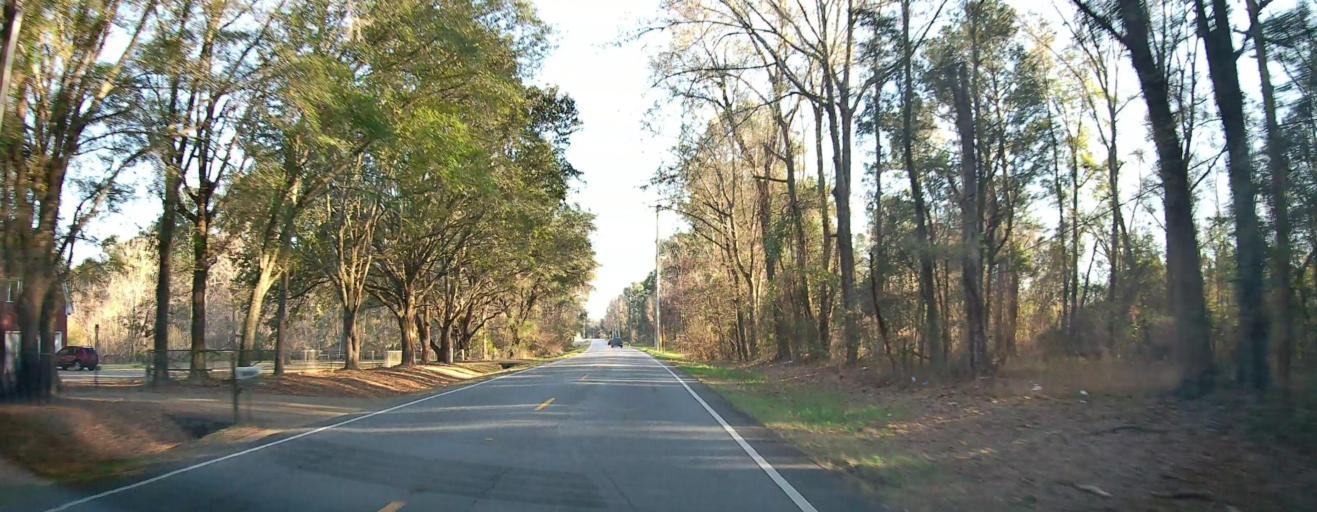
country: US
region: Georgia
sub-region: Dougherty County
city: Albany
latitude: 31.6209
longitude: -84.1621
